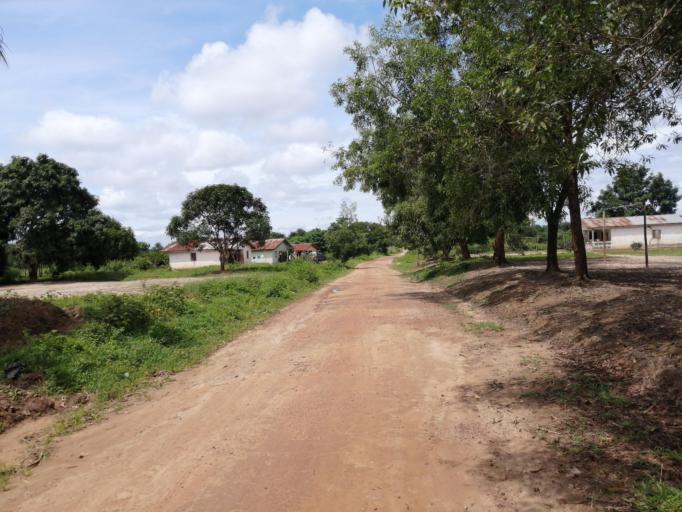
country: SL
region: Northern Province
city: Pepel
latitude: 8.6861
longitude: -12.9985
